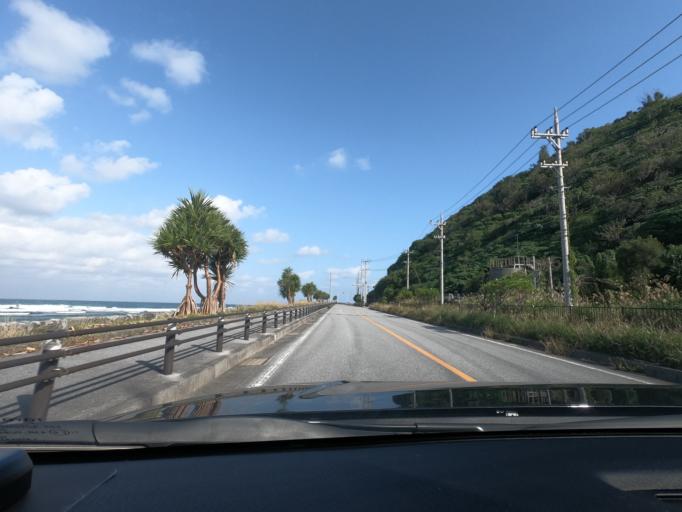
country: JP
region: Okinawa
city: Nago
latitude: 26.7586
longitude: 128.1893
